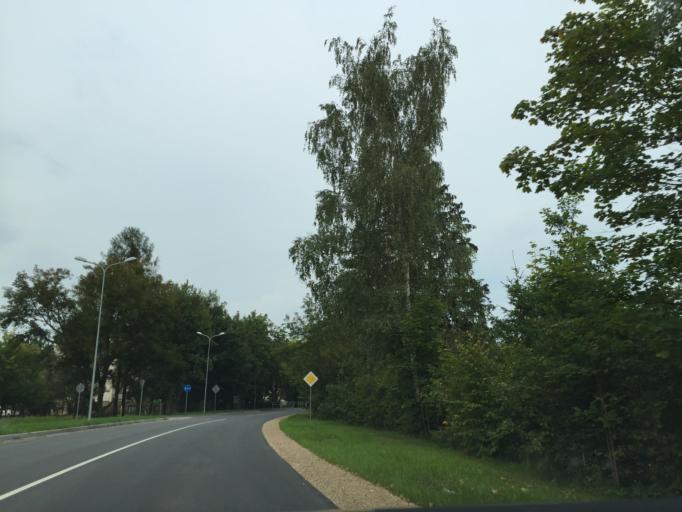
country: LV
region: Ogre
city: Ogre
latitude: 56.8181
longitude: 24.6533
